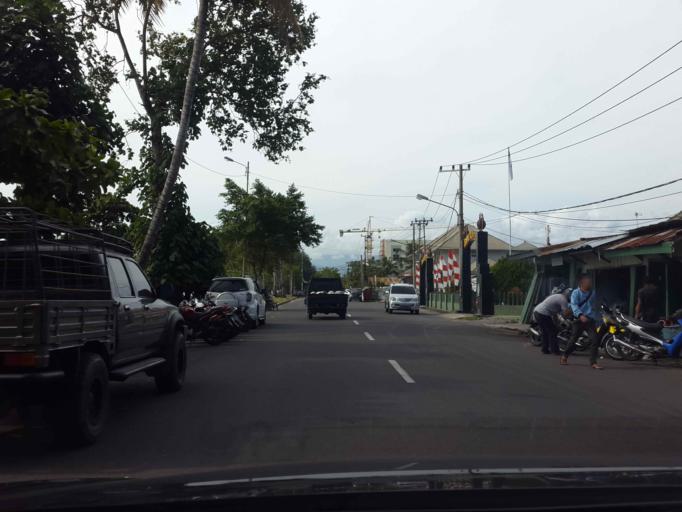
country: ID
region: West Sumatra
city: Padang
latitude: -0.9635
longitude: 100.3523
